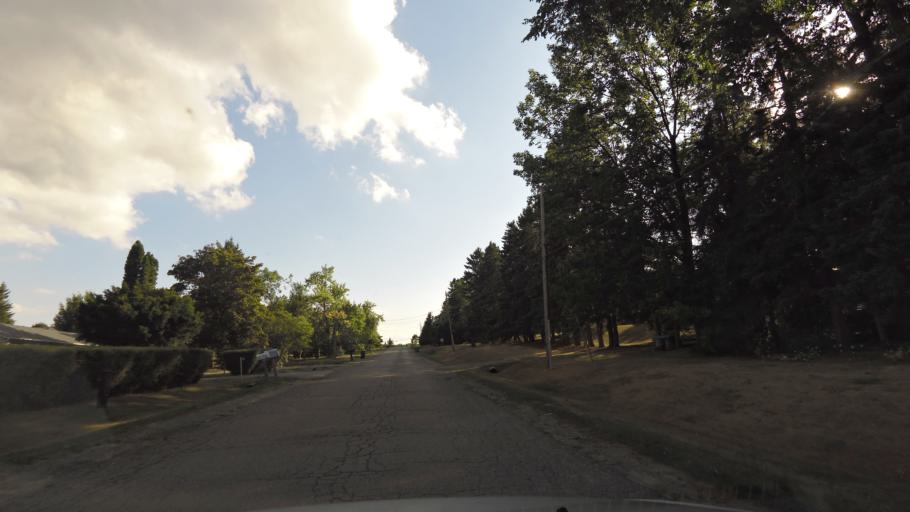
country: CA
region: Ontario
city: Brampton
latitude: 43.7604
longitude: -79.9292
